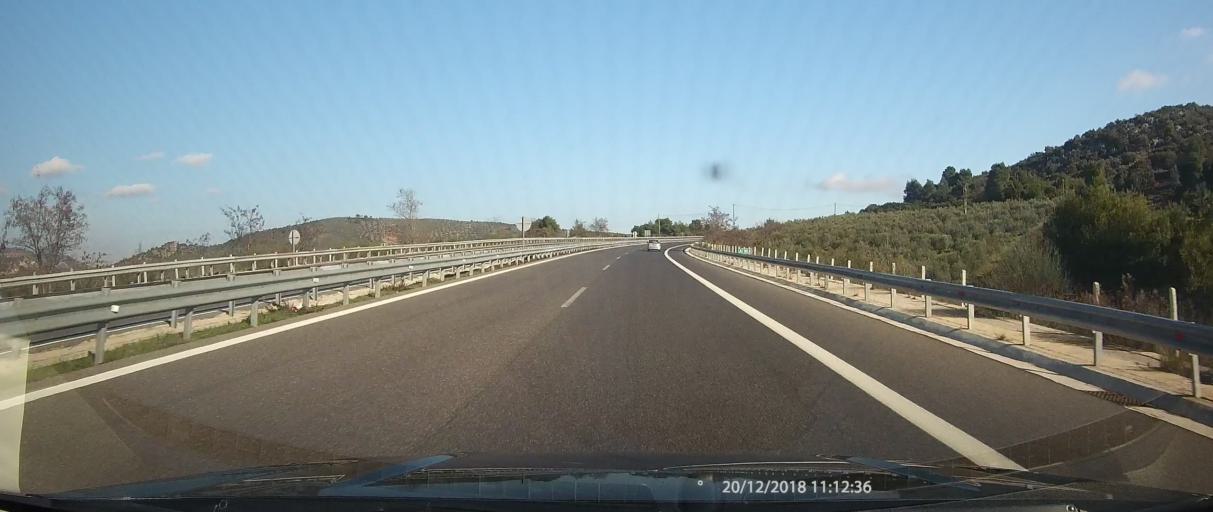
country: GR
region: Peloponnese
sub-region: Nomos Korinthias
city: Ayios Vasilios
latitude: 37.8431
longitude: 22.8132
